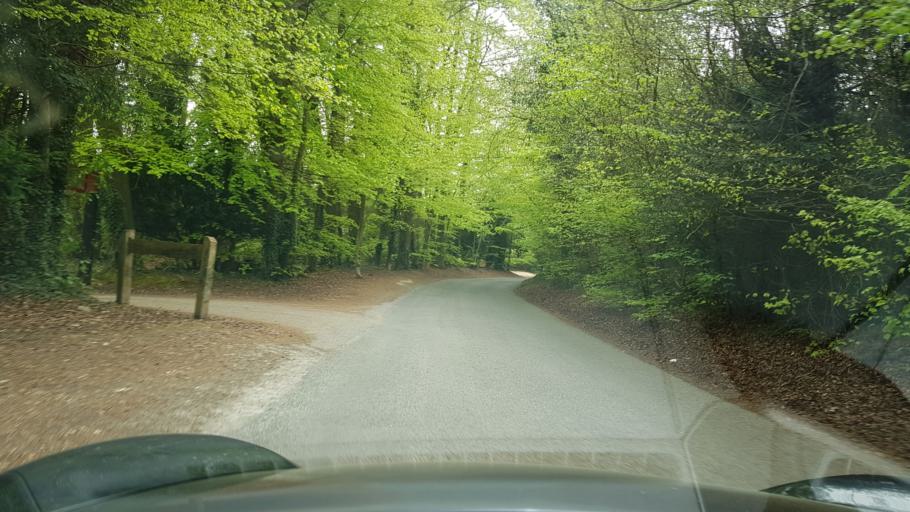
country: GB
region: England
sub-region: Surrey
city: East Horsley
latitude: 51.2520
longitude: -0.4475
